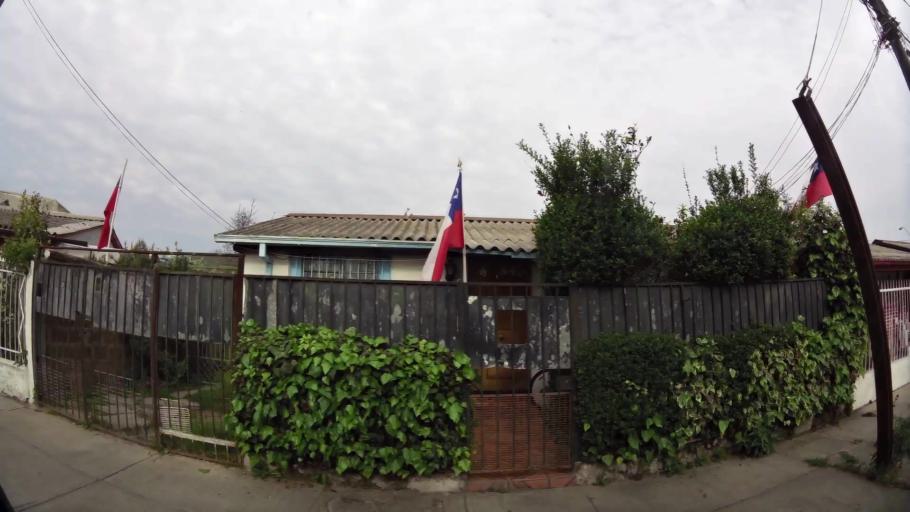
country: CL
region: Santiago Metropolitan
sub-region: Provincia de Santiago
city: Lo Prado
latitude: -33.5144
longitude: -70.7533
